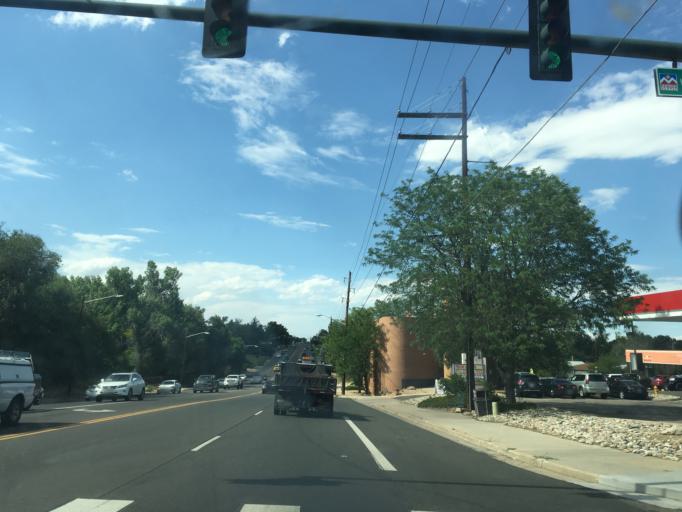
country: US
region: Colorado
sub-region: Jefferson County
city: Lakewood
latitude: 39.6822
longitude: -105.0532
